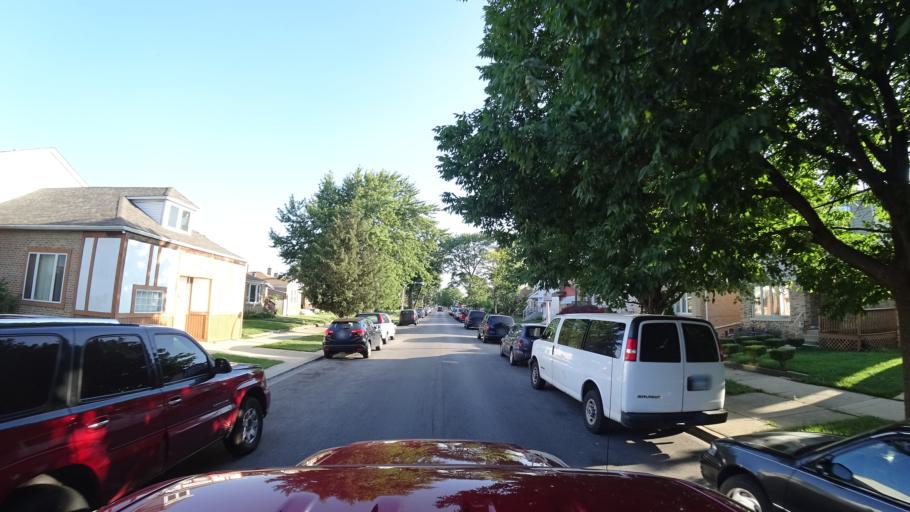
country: US
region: Illinois
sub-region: Cook County
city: Hometown
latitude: 41.7846
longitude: -87.7352
